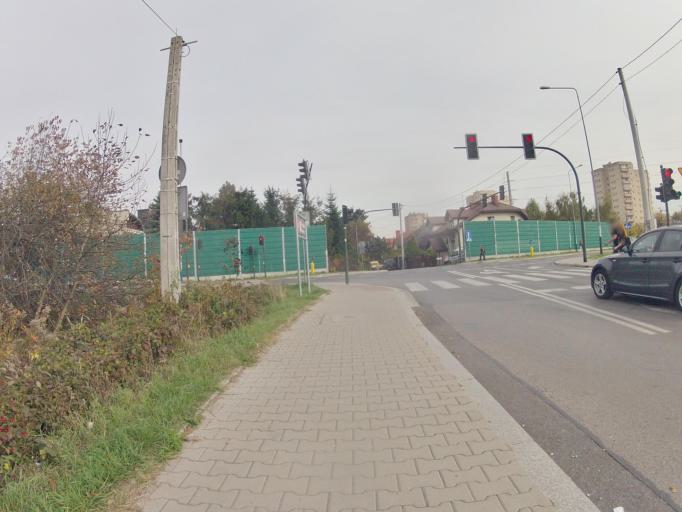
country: PL
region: Lesser Poland Voivodeship
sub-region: Krakow
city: Krakow
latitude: 50.0306
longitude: 19.9114
